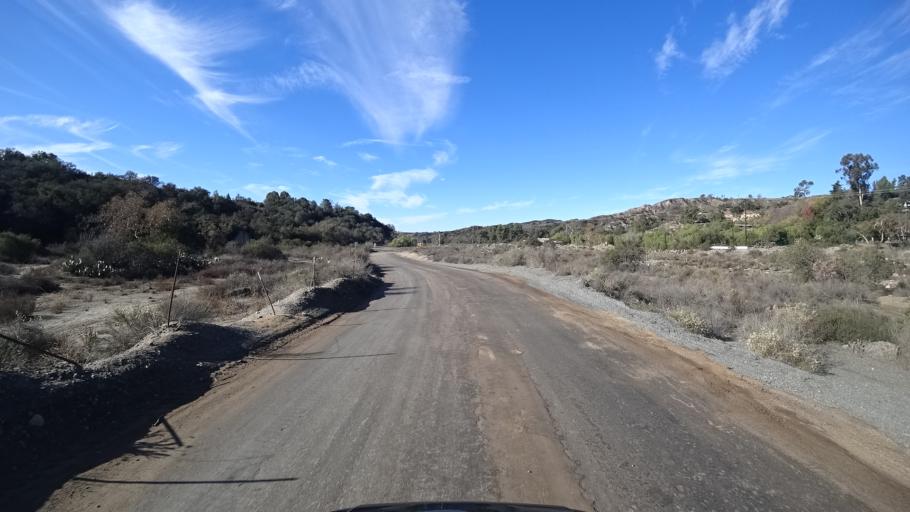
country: US
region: California
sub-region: Orange County
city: Trabuco Canyon
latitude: 33.6600
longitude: -117.5840
